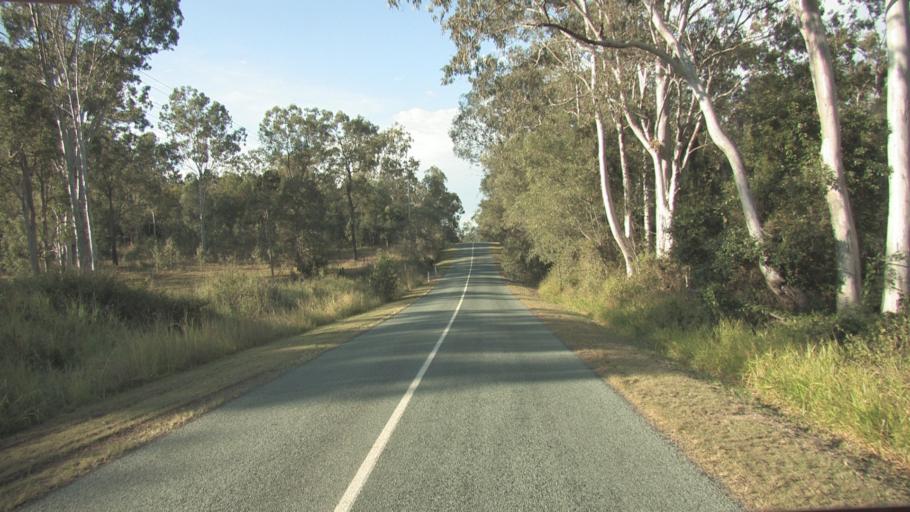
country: AU
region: Queensland
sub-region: Gold Coast
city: Ormeau Hills
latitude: -27.8404
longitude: 153.1640
